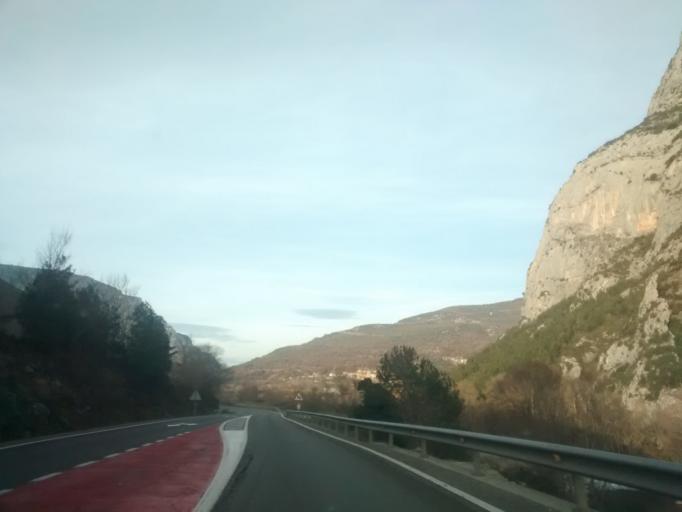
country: ES
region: Catalonia
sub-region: Provincia de Lleida
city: Coll de Nargo
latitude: 42.1867
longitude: 1.3306
